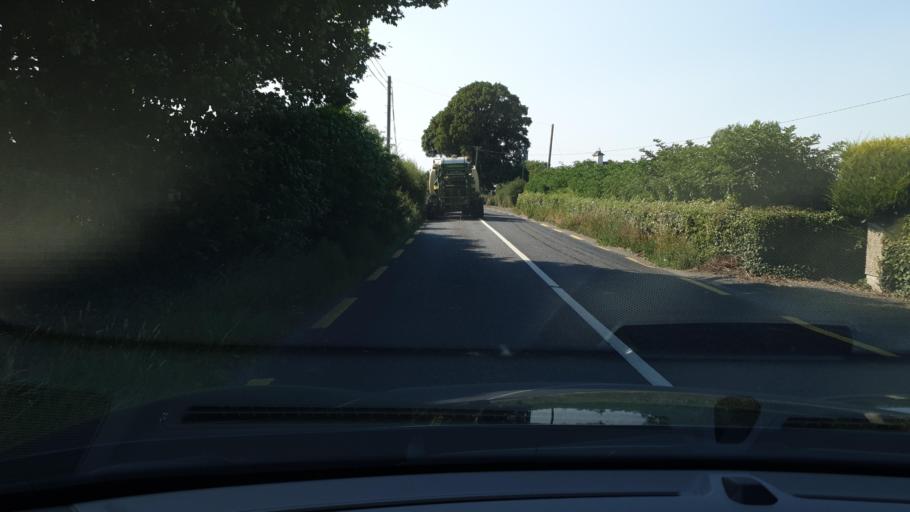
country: IE
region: Leinster
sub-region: An Mhi
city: Trim
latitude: 53.5826
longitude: -6.8508
